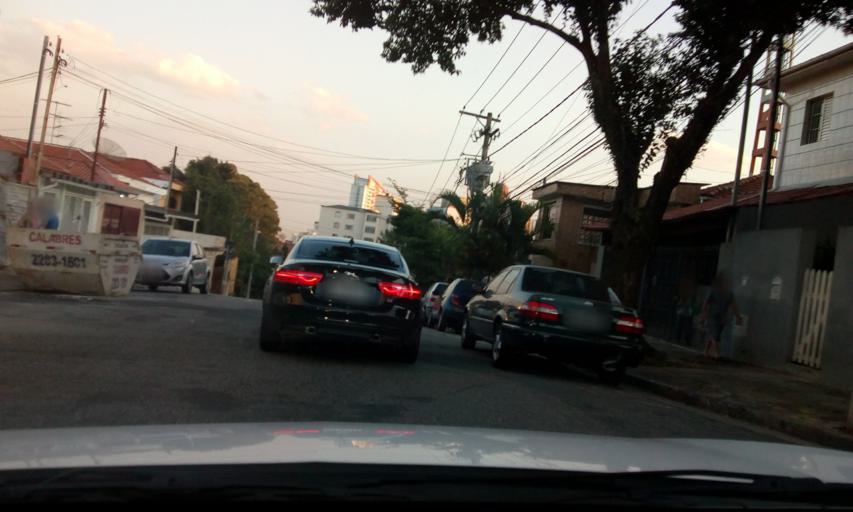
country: BR
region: Sao Paulo
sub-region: Sao Paulo
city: Sao Paulo
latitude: -23.4892
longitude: -46.6124
